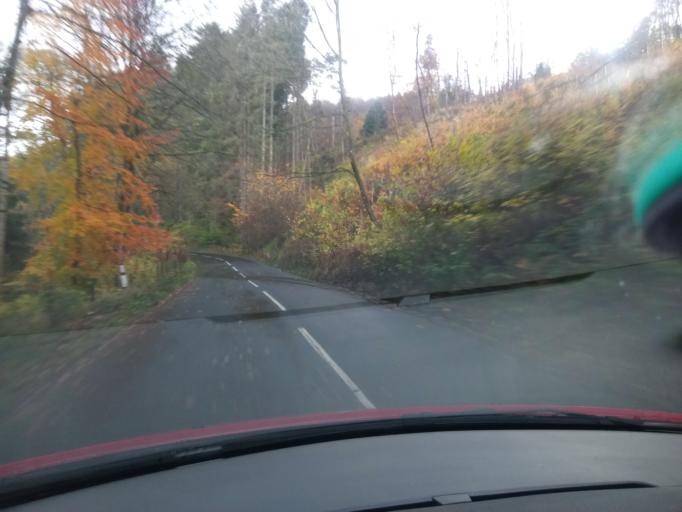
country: GB
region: England
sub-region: Northumberland
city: Birtley
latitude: 55.1034
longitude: -2.2355
